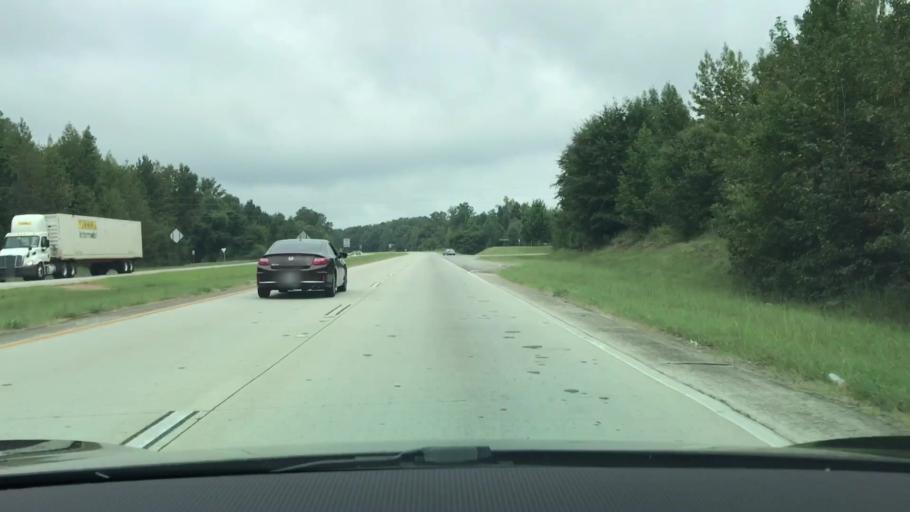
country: US
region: Georgia
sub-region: Oconee County
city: Bogart
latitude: 33.9130
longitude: -83.4686
